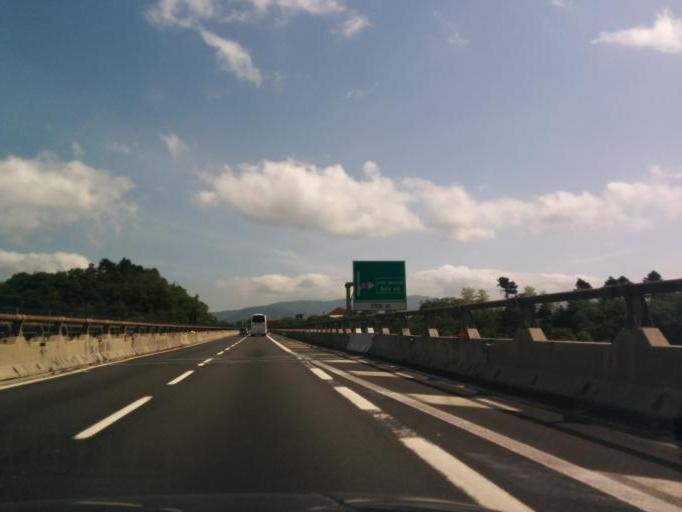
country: IT
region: Tuscany
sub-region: Province of Florence
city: Barberino di Mugello
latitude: 44.0269
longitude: 11.2231
